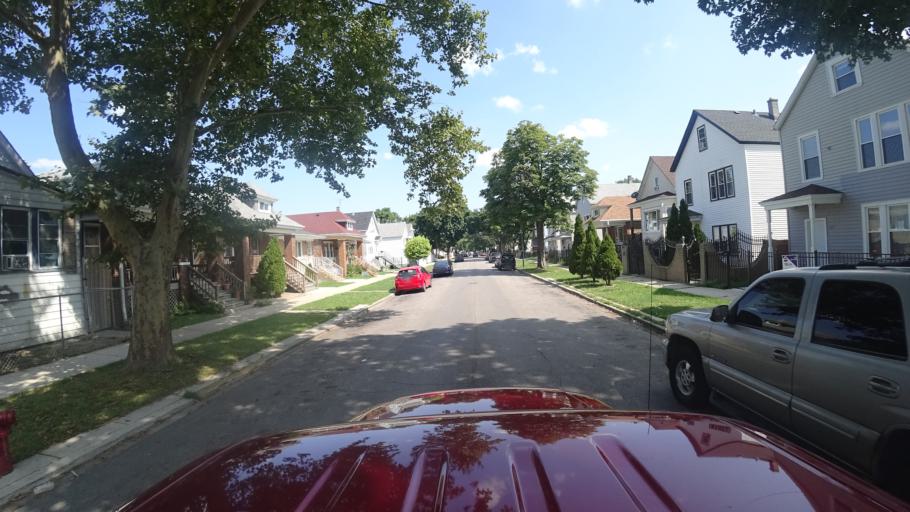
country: US
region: Illinois
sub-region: Cook County
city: Chicago
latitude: 41.7983
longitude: -87.6878
